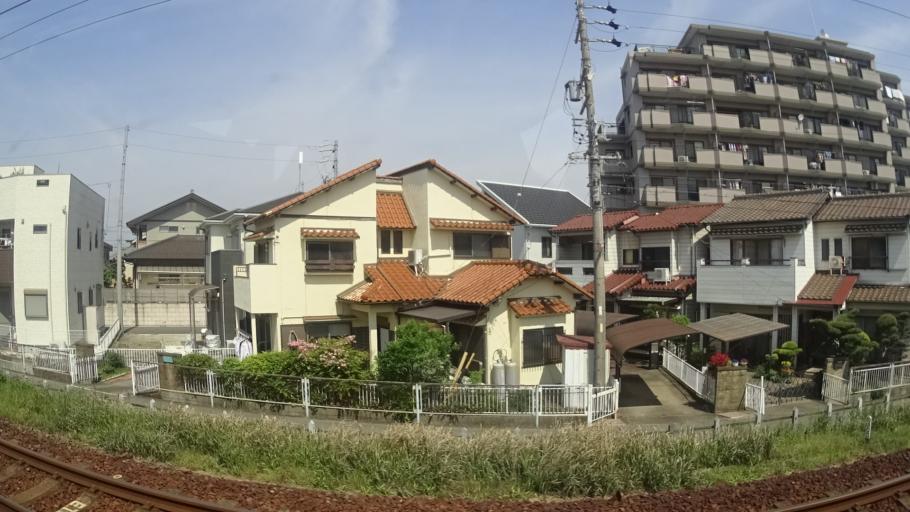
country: JP
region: Aichi
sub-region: Aisai-shi
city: Aisai
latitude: 35.1119
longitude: 136.7213
